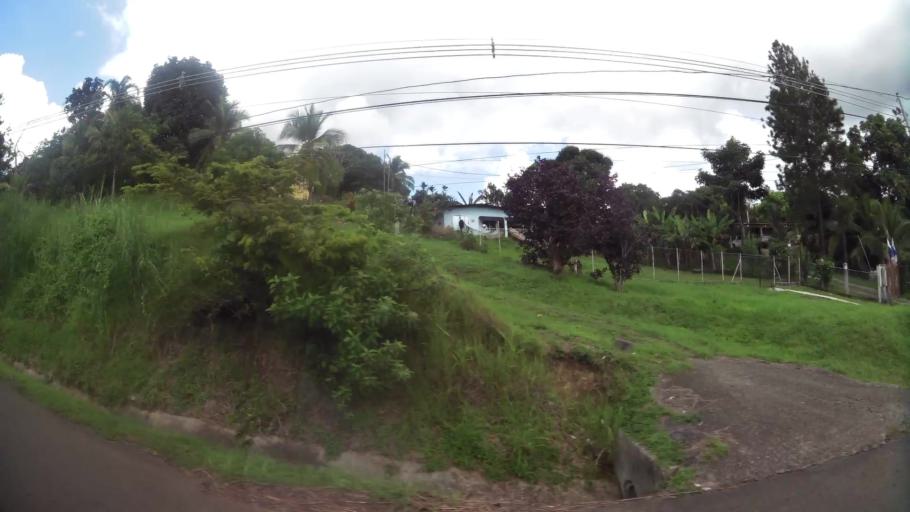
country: PA
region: Panama
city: Nuevo Arraijan
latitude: 8.9243
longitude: -79.7346
